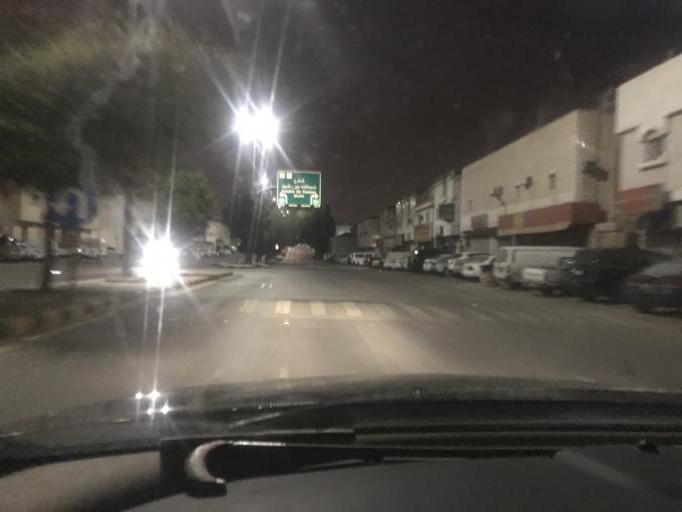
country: SA
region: Ar Riyad
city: Riyadh
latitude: 24.7289
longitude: 46.7638
